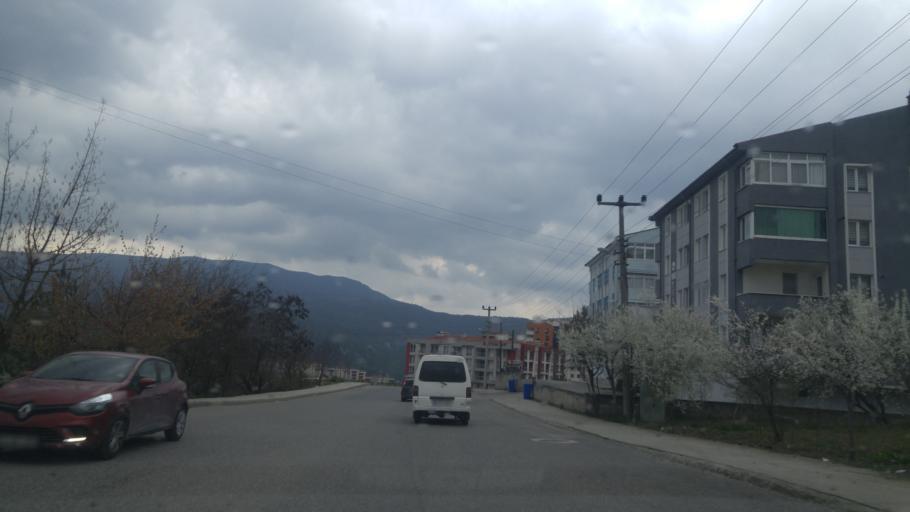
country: TR
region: Karabuk
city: Safranbolu
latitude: 41.2234
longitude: 32.6723
